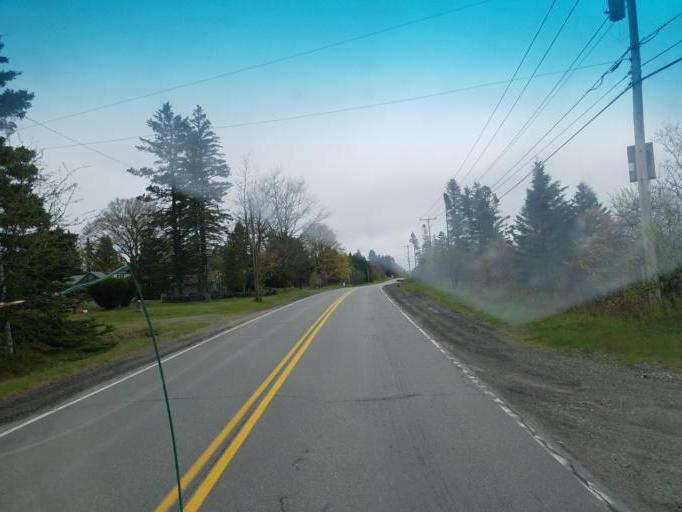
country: US
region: Maine
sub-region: Washington County
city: Eastport
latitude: 44.8247
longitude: -67.0461
